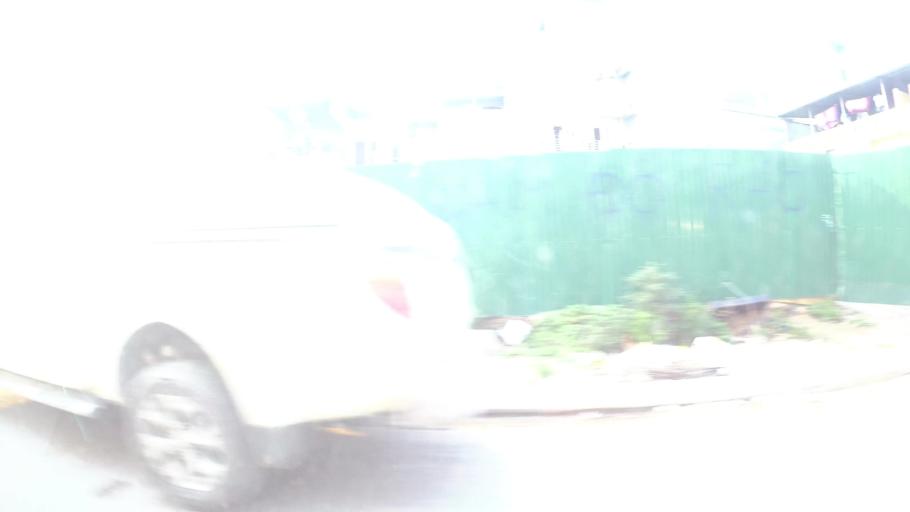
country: VN
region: Ha Noi
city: Thanh Xuan
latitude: 20.9759
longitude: 105.8194
